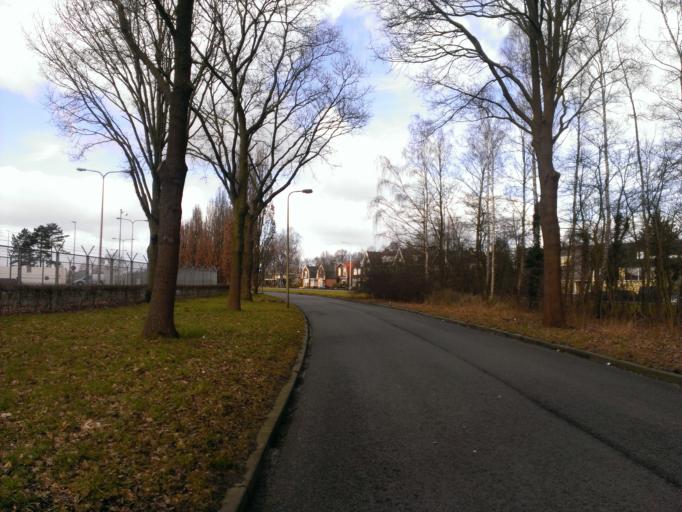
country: NL
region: Overijssel
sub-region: Gemeente Almelo
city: Almelo
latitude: 52.3393
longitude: 6.6931
